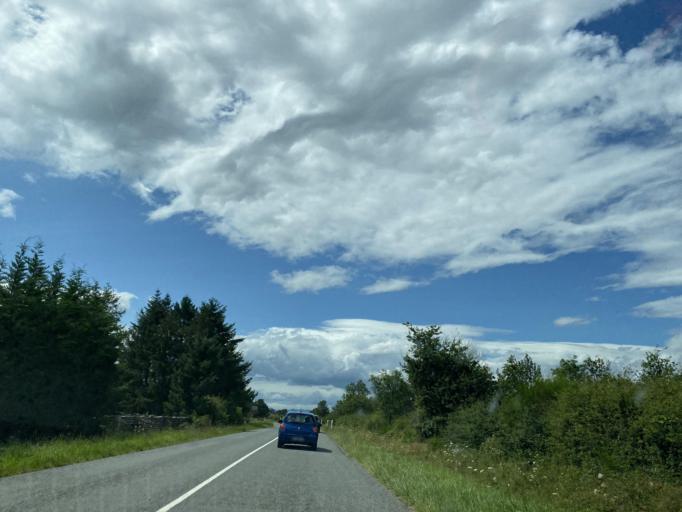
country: FR
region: Auvergne
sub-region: Departement du Puy-de-Dome
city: Peschadoires
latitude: 45.7908
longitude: 3.4637
